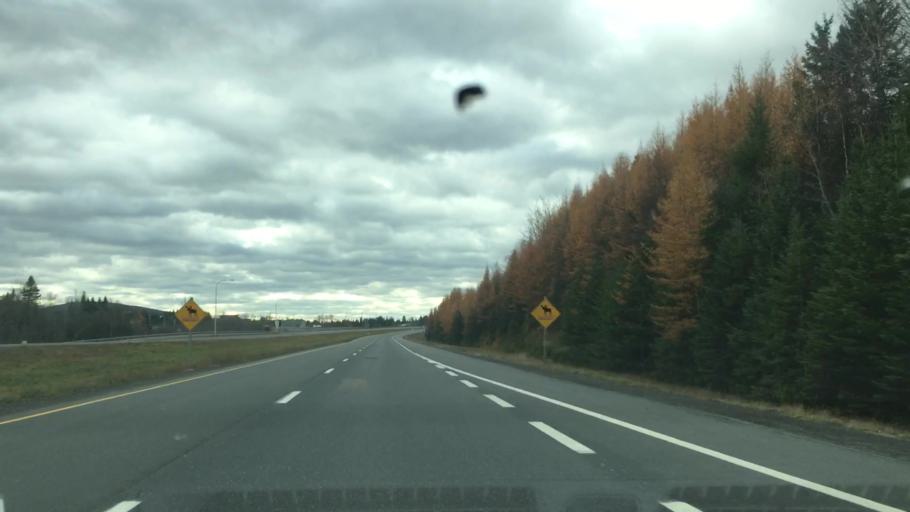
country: US
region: Maine
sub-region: Aroostook County
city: Fort Fairfield
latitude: 46.7459
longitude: -67.7149
